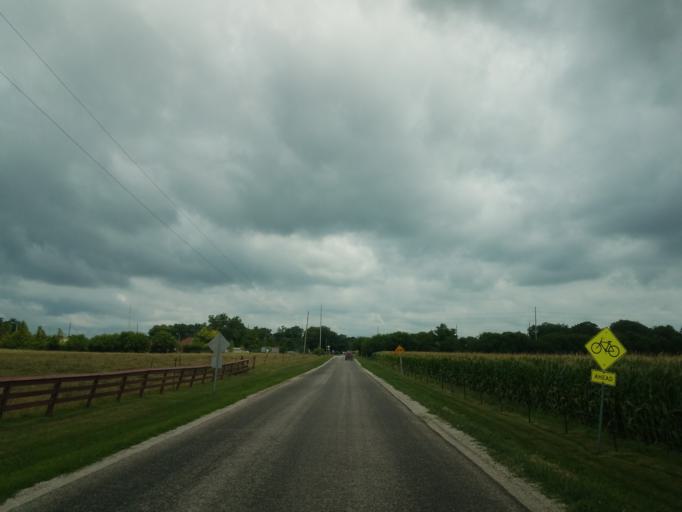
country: US
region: Illinois
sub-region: McLean County
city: Bloomington
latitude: 40.4770
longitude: -89.0329
